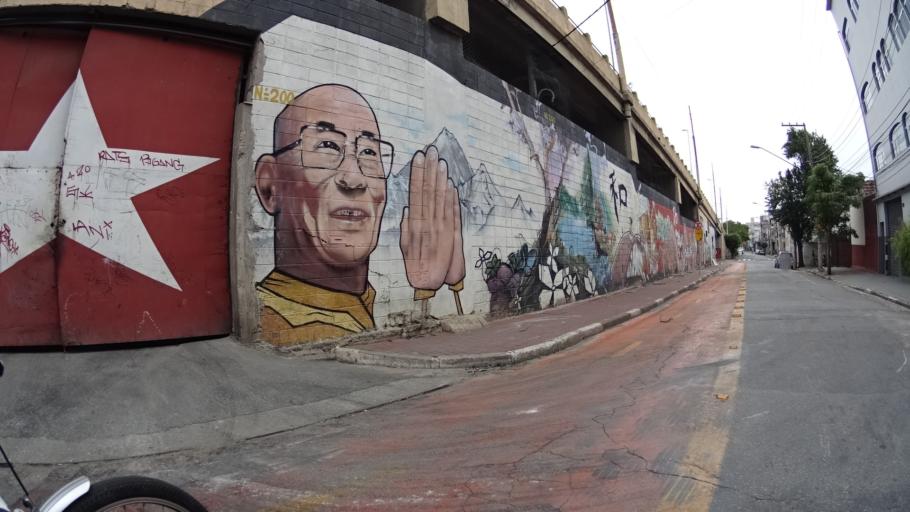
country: BR
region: Sao Paulo
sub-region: Sao Paulo
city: Sao Paulo
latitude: -23.5266
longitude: -46.6483
